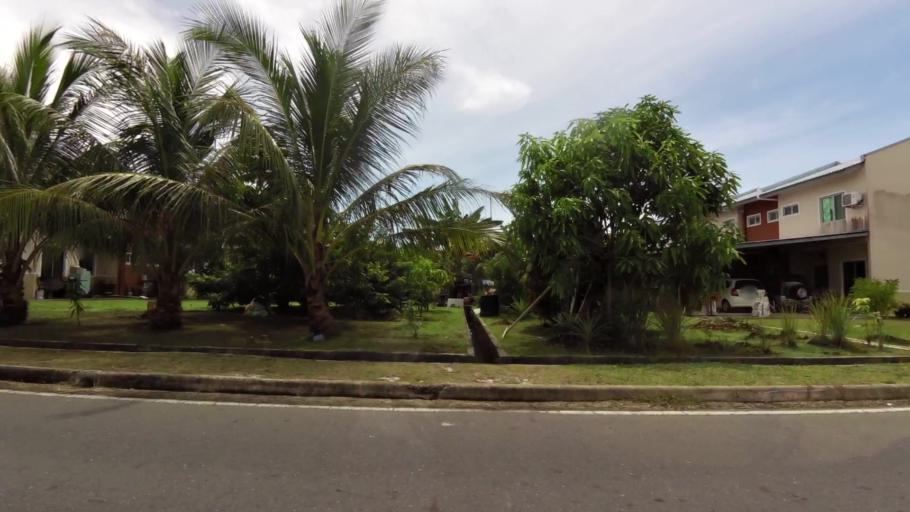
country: BN
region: Belait
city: Kuala Belait
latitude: 4.5894
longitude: 114.2744
